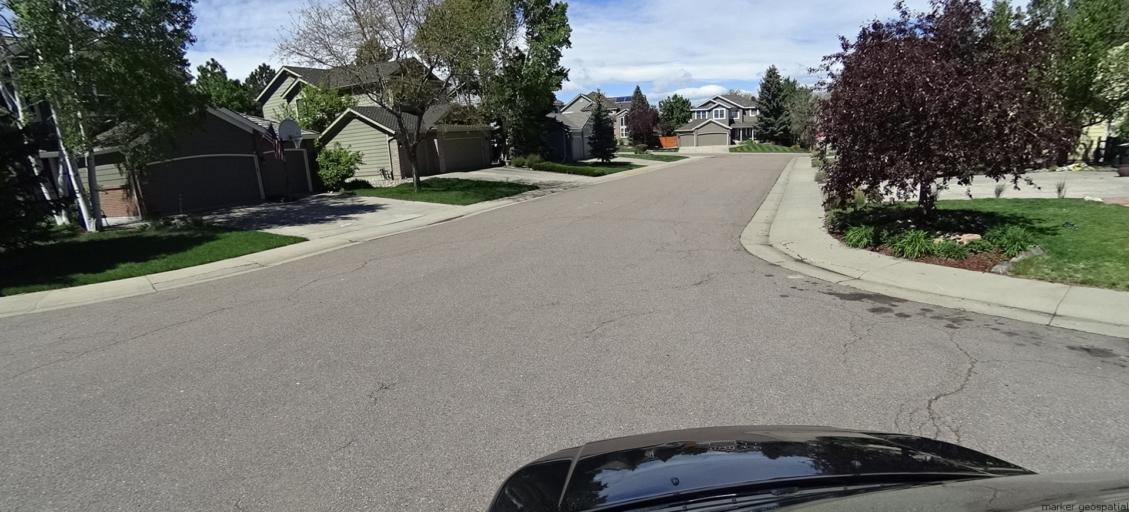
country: US
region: Colorado
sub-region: Adams County
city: Lone Tree
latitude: 39.5465
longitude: -104.8941
